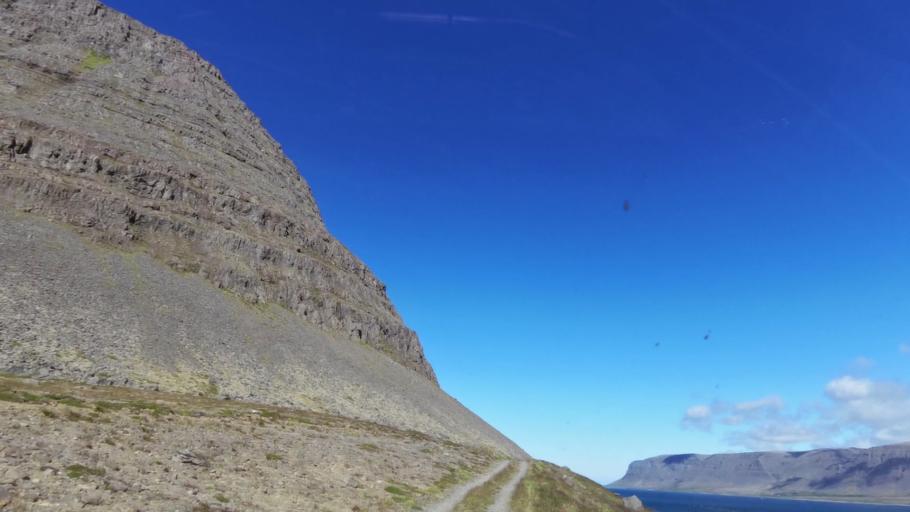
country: IS
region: West
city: Olafsvik
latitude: 65.6259
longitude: -23.8987
